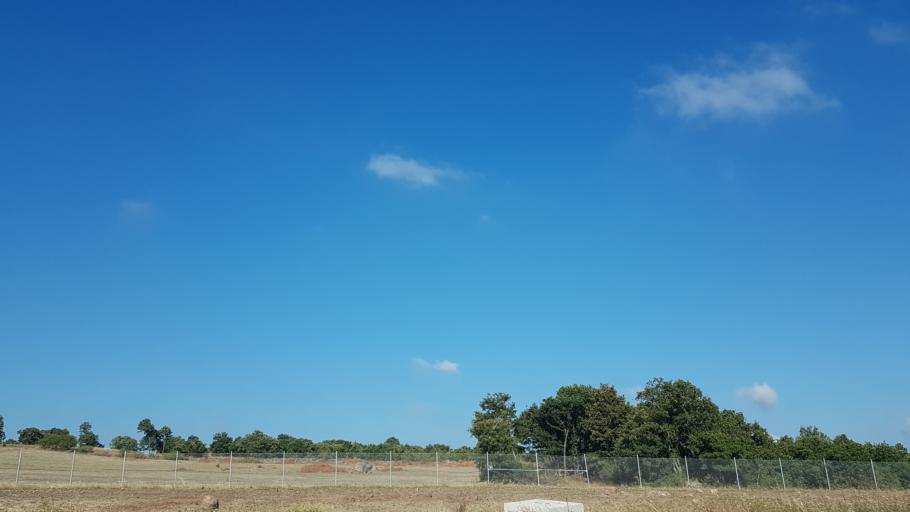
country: TR
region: Balikesir
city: Ertugrul
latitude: 39.5358
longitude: 27.6754
